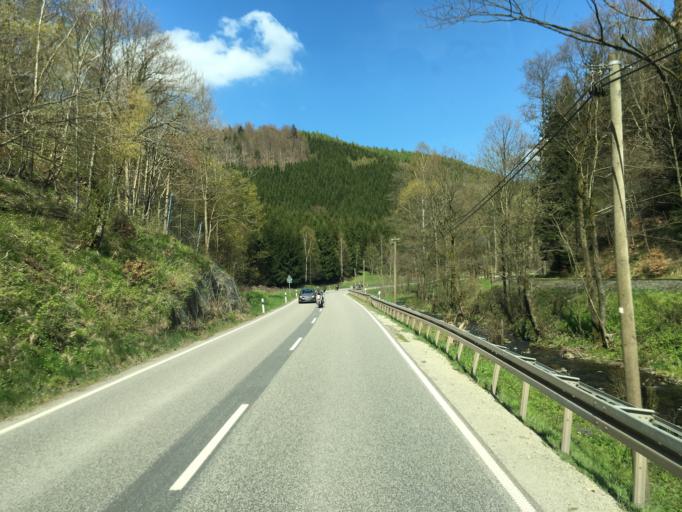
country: DE
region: Thuringia
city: Ilfeld
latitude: 51.6170
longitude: 10.8007
